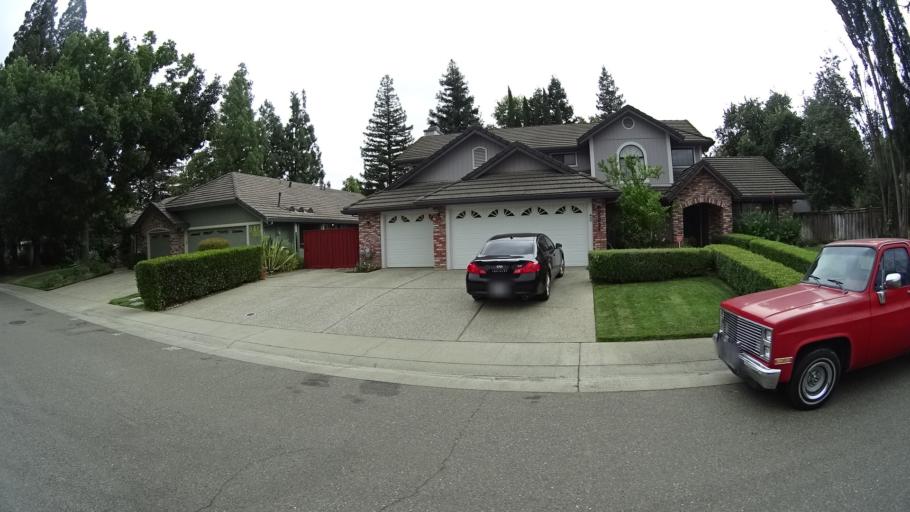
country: US
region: California
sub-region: Sacramento County
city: Laguna
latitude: 38.4171
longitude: -121.4437
